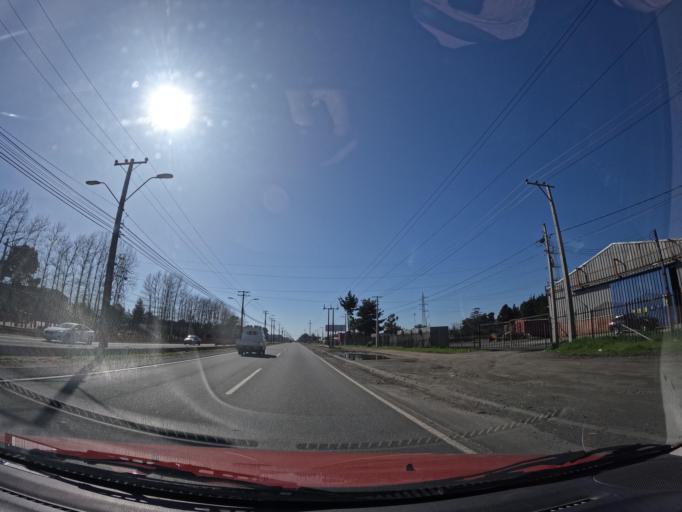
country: CL
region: Biobio
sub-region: Provincia de Concepcion
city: Coronel
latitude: -36.9360
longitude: -73.1522
